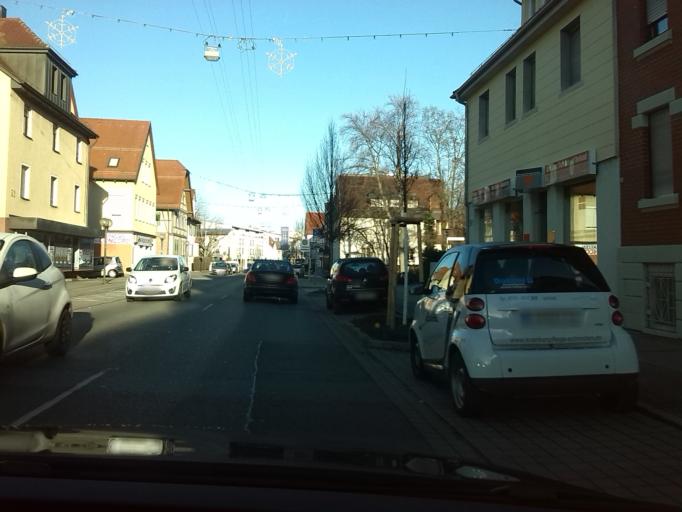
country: DE
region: Baden-Wuerttemberg
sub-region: Regierungsbezirk Stuttgart
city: Fellbach
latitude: 48.8295
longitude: 9.2653
